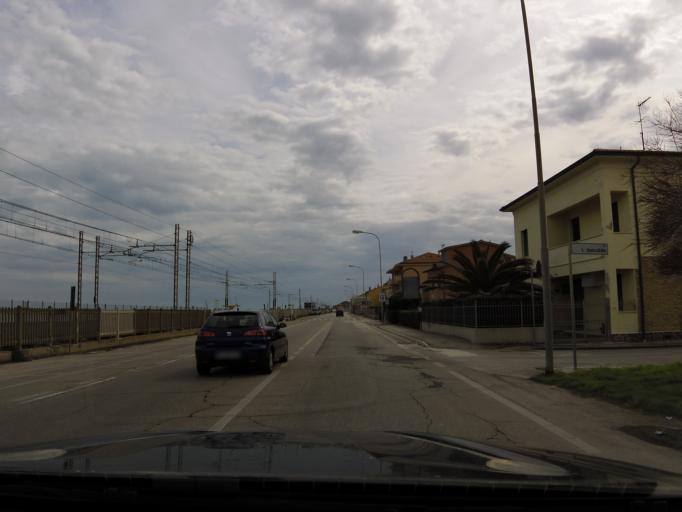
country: IT
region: The Marches
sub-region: Provincia di Macerata
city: Porto Potenza Picena
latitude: 43.3362
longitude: 13.7097
